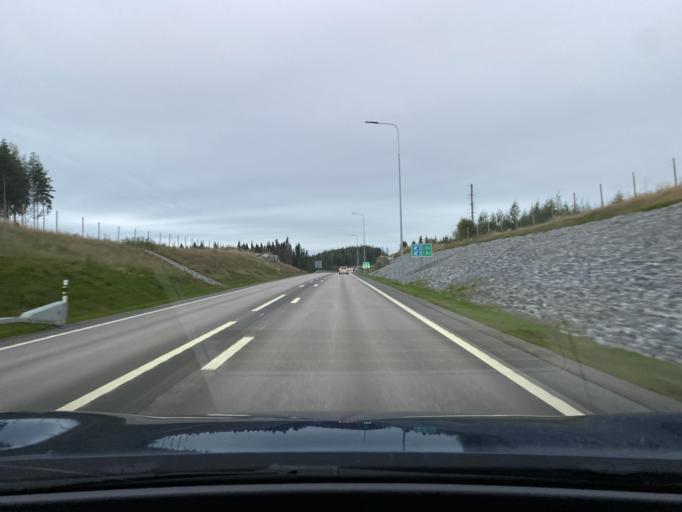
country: FI
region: Paijanne Tavastia
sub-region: Lahti
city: Hollola
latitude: 60.9596
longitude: 25.5439
